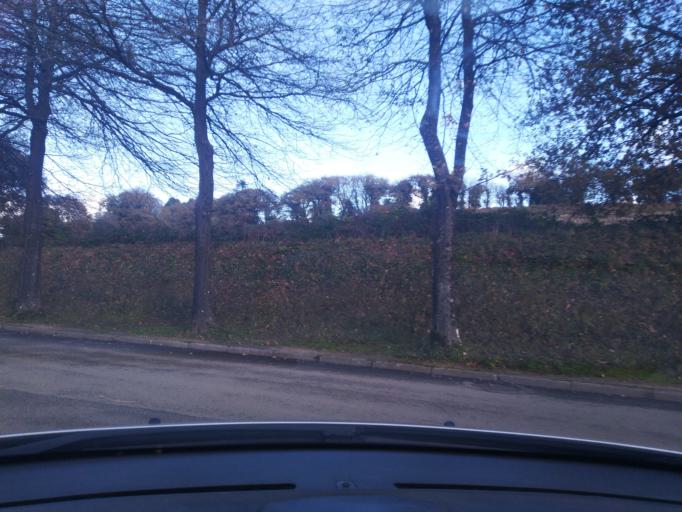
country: FR
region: Brittany
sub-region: Departement du Finistere
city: Guerlesquin
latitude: 48.5137
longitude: -3.5841
